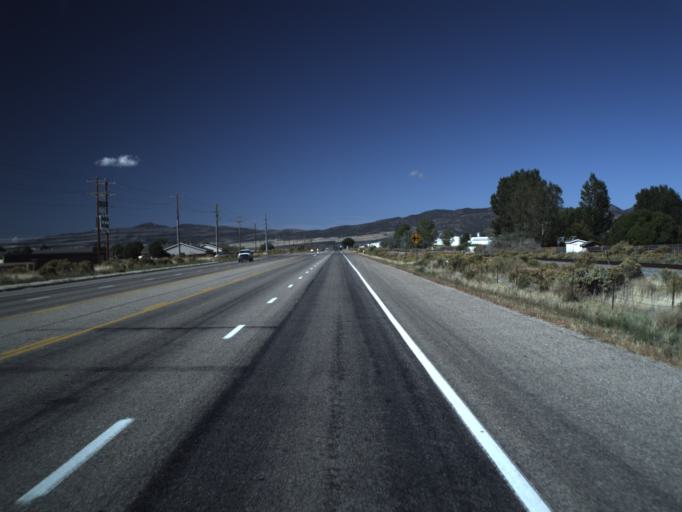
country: US
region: Utah
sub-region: Iron County
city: Cedar City
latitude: 37.6851
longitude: -113.1332
